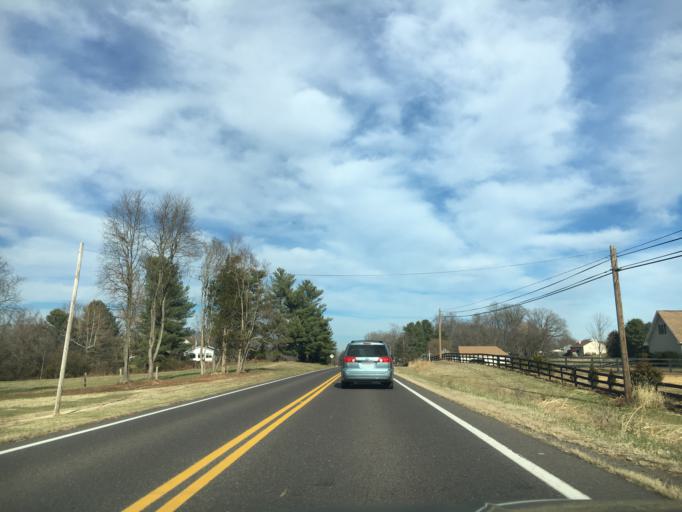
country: US
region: Virginia
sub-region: Culpeper County
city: Culpeper
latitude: 38.5247
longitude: -77.9831
